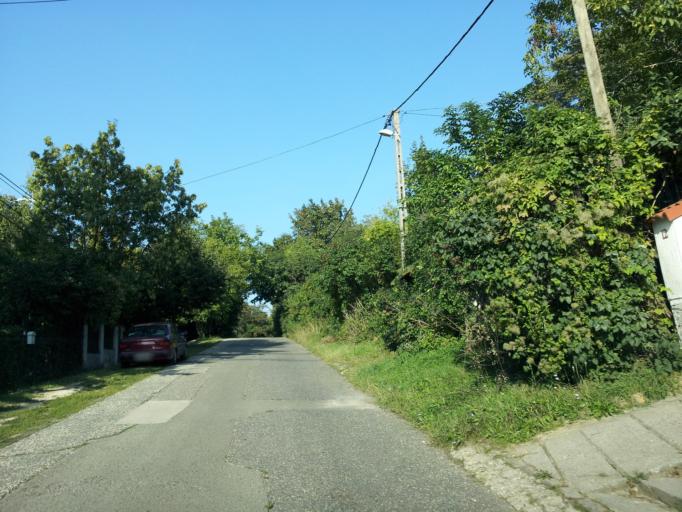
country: HU
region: Pest
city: Solymar
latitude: 47.5529
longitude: 18.9666
